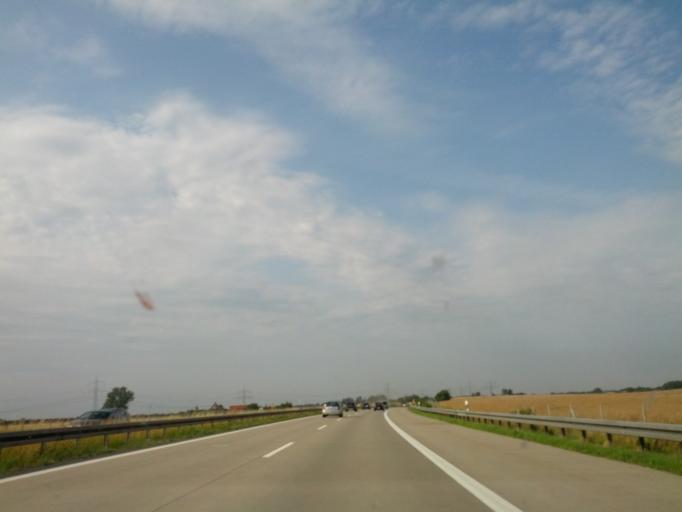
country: DE
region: Mecklenburg-Vorpommern
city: Kavelstorf
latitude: 53.9836
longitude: 12.1963
